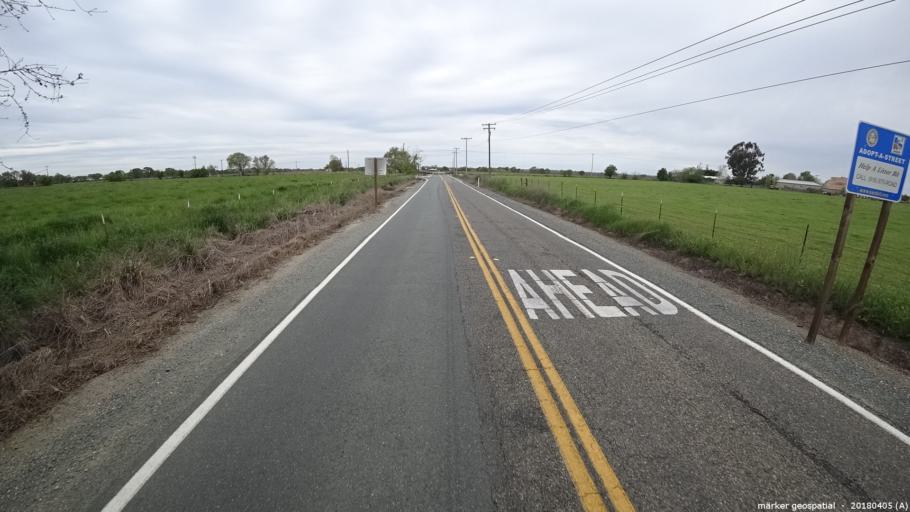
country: US
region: California
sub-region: San Joaquin County
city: Thornton
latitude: 38.2472
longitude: -121.3672
